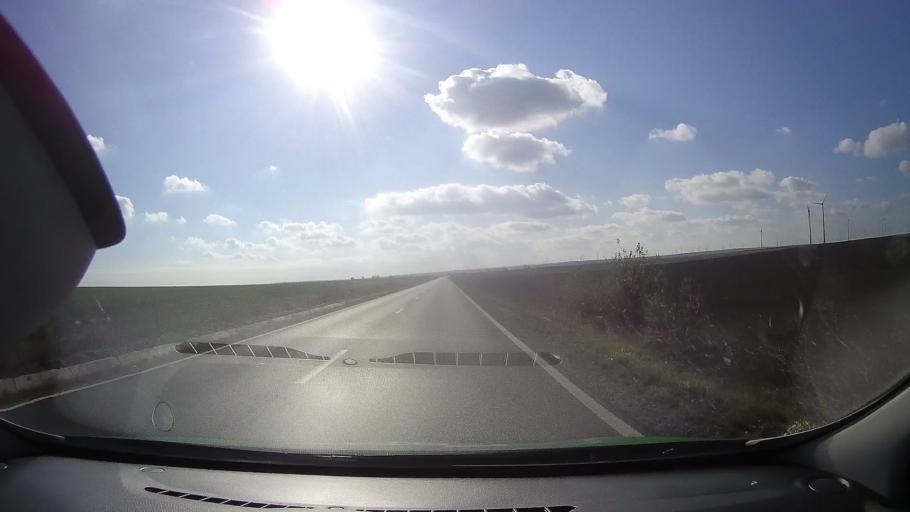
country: RO
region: Constanta
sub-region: Comuna Mihai Viteazu
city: Mihai Viteazu
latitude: 44.6717
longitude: 28.6840
